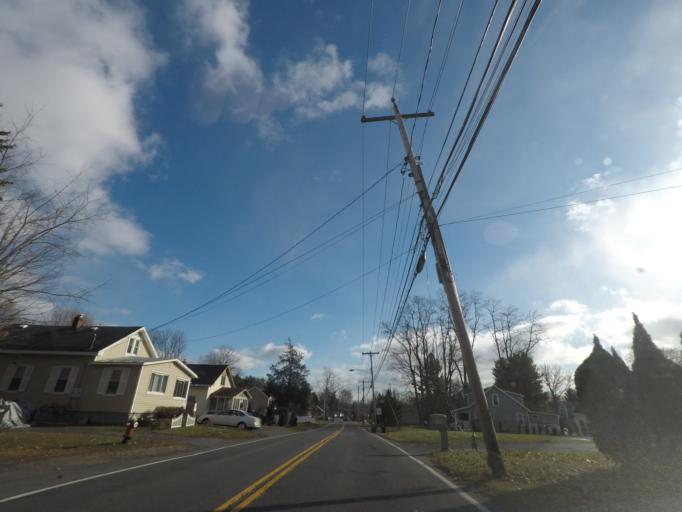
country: US
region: New York
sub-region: Schenectady County
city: Niskayuna
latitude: 42.7539
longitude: -73.8791
